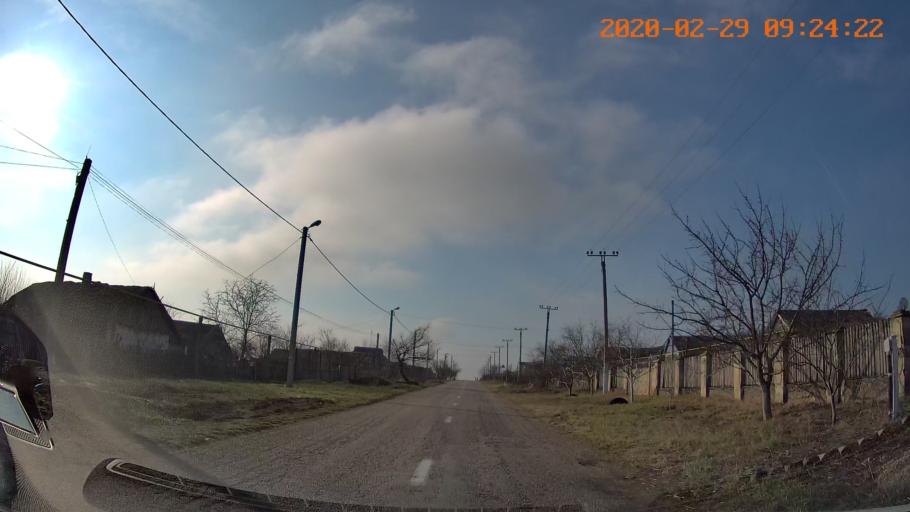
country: MD
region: Telenesti
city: Pervomaisc
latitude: 46.7169
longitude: 29.9588
